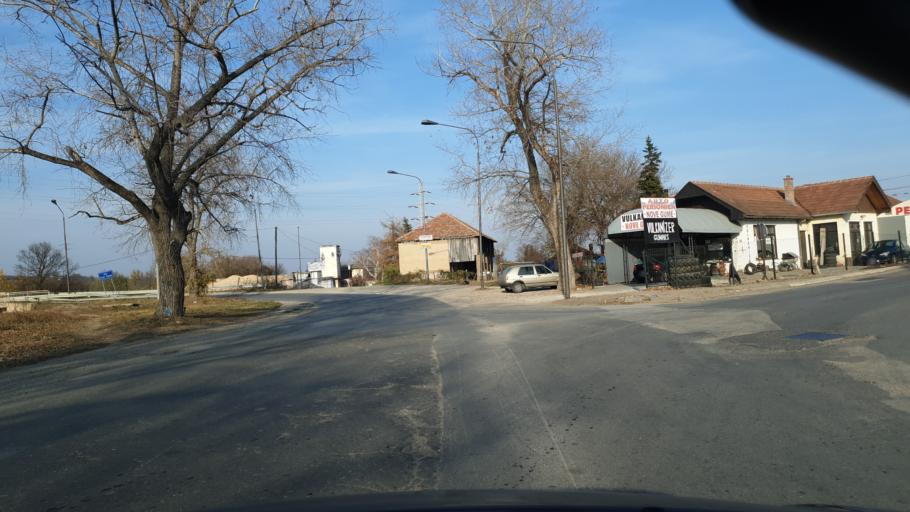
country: RS
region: Central Serbia
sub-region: Zajecarski Okrug
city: Zajecar
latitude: 43.9122
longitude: 22.2921
